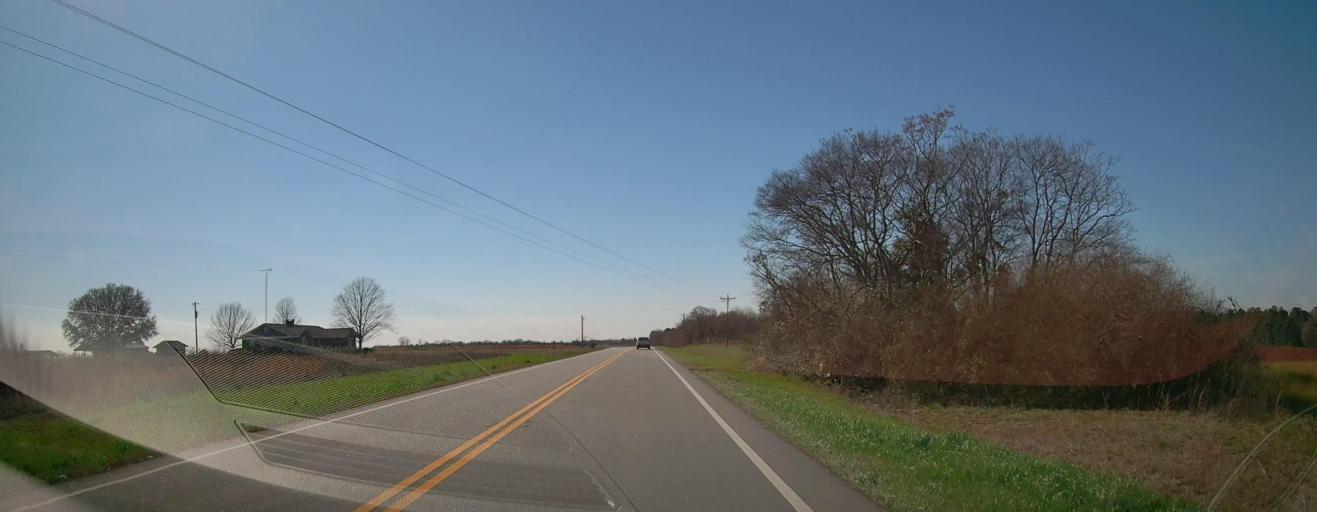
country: US
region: Georgia
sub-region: Dooly County
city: Unadilla
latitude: 32.3377
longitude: -83.8198
